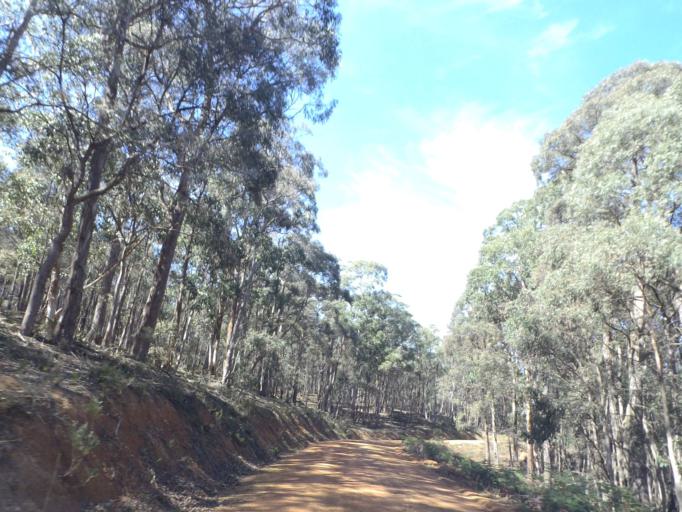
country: AU
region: Victoria
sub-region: Moorabool
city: Bacchus Marsh
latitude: -37.4348
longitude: 144.3714
